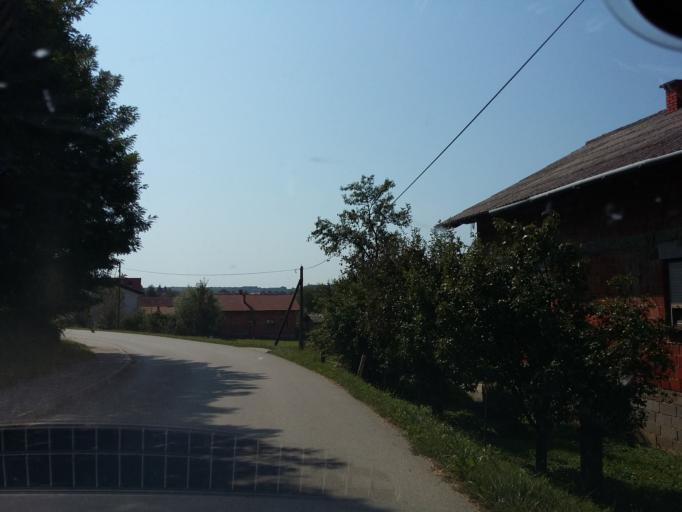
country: SI
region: Hodos-Hodos
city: Hodos
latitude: 46.8300
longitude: 16.3226
